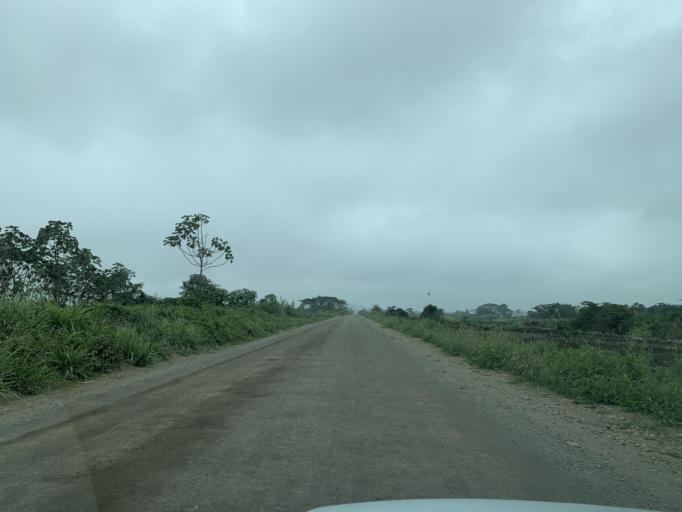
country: EC
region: Guayas
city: Coronel Marcelino Mariduena
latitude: -2.3598
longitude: -79.5808
